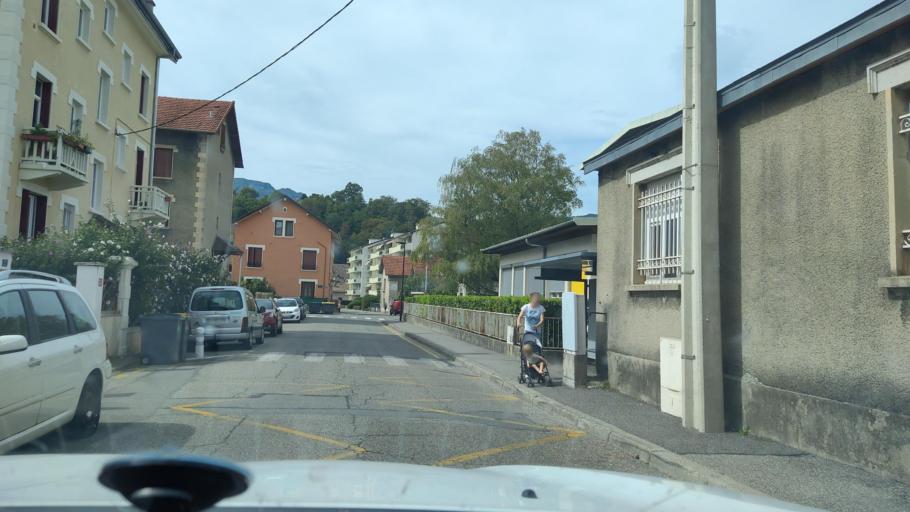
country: FR
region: Rhone-Alpes
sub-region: Departement de la Savoie
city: Tresserve
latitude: 45.6900
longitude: 5.9069
